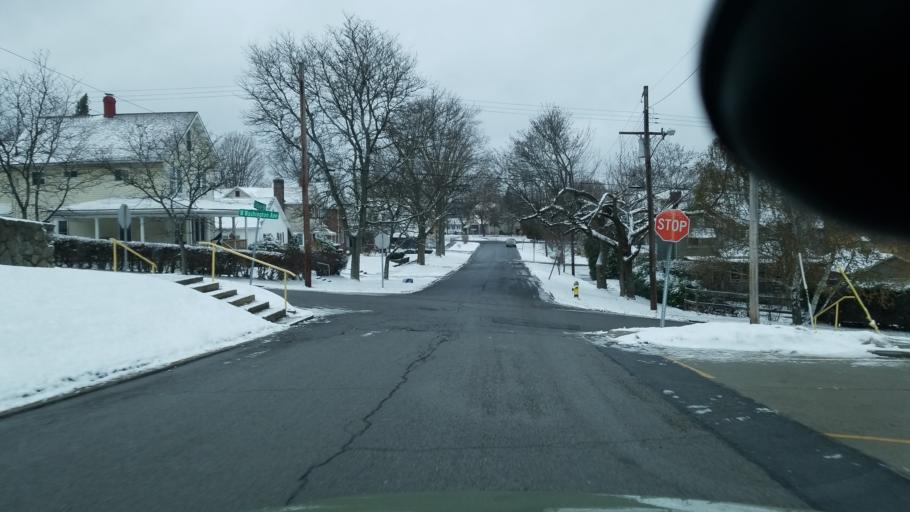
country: US
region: Pennsylvania
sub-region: Clearfield County
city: DuBois
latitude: 41.1210
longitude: -78.7696
